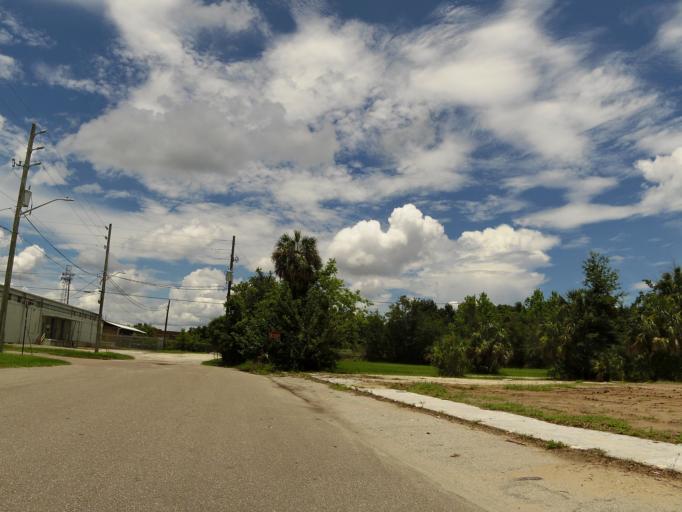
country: US
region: Florida
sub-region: Duval County
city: Jacksonville
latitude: 30.3495
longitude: -81.6475
